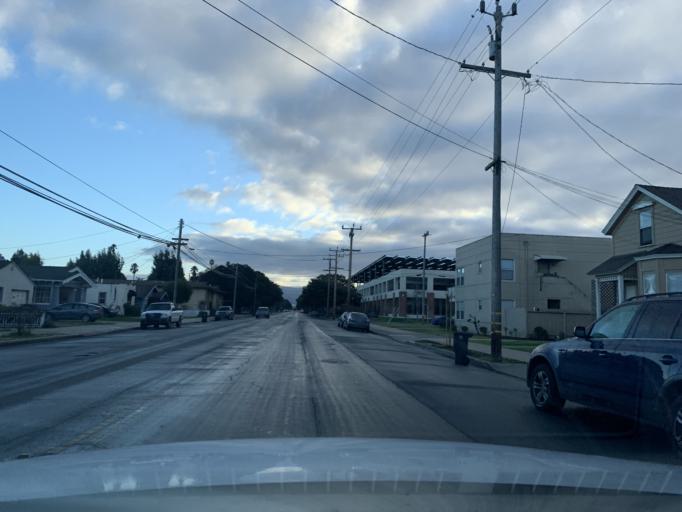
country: US
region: California
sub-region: Monterey County
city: Salinas
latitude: 36.6750
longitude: -121.6691
